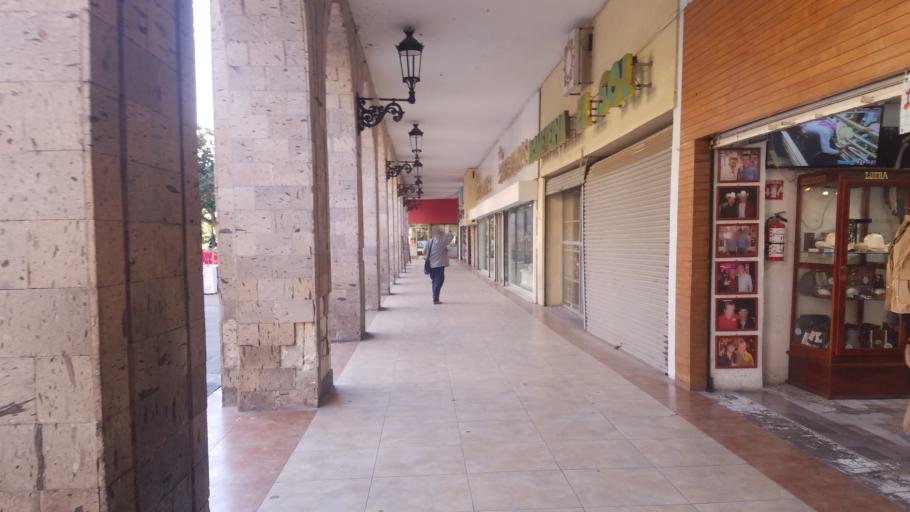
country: MX
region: Jalisco
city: Guadalajara
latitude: 20.6771
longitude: -103.3427
